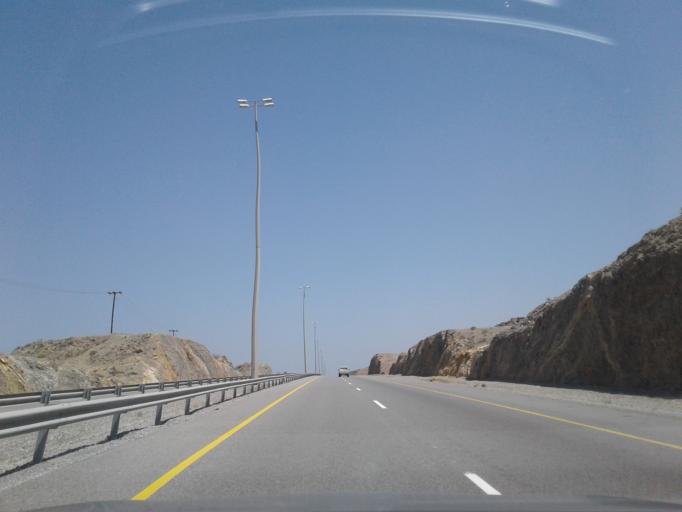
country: OM
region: Muhafazat Masqat
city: Muscat
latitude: 23.2043
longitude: 58.8169
